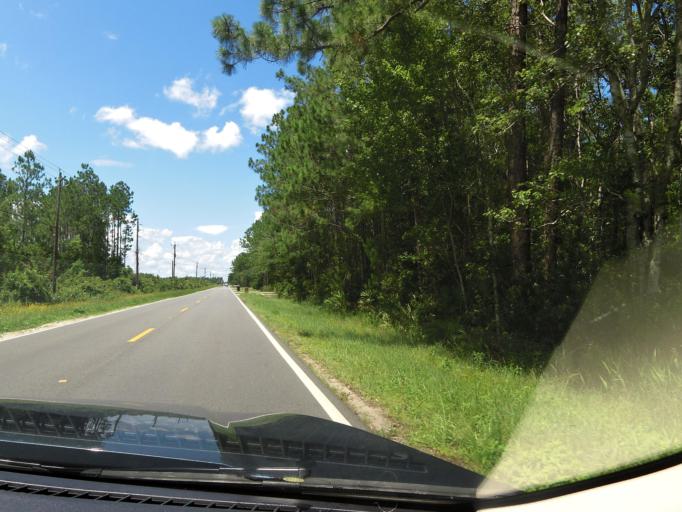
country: US
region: Florida
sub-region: Nassau County
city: Yulee
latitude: 30.6493
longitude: -81.5437
